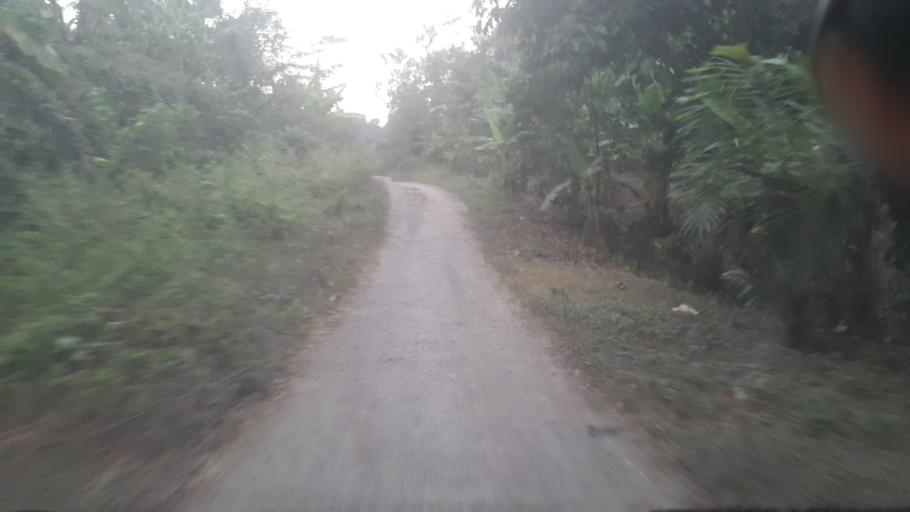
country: ID
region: West Java
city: Bojonggaling
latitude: -6.9624
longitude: 106.6035
